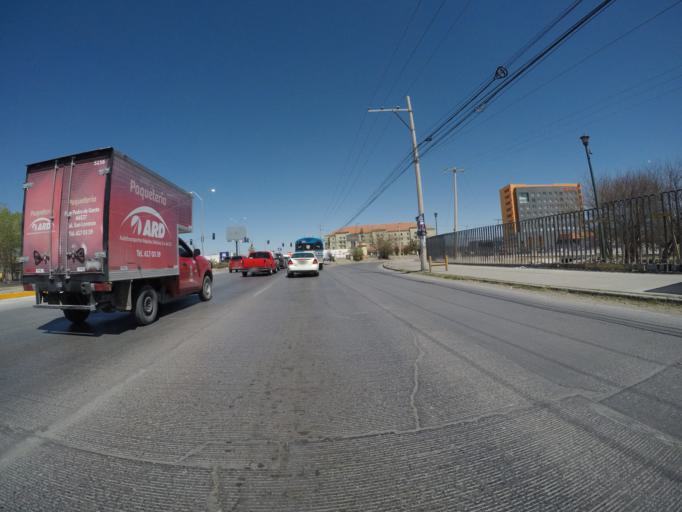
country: MX
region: Chihuahua
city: Ciudad Juarez
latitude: 31.6896
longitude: -106.4244
